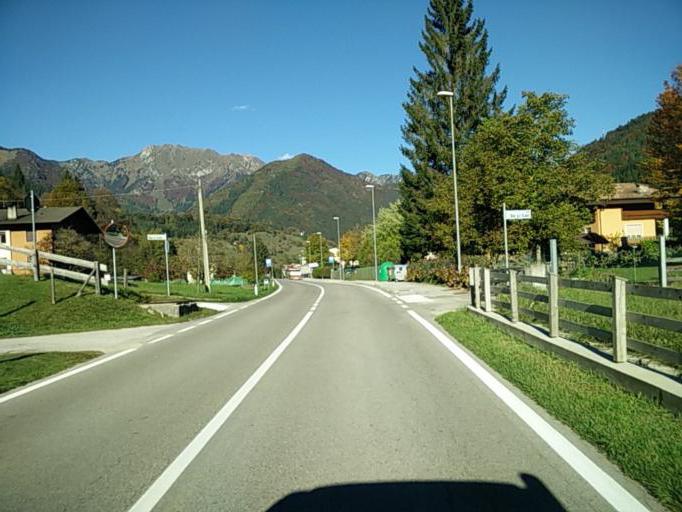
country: IT
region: Trentino-Alto Adige
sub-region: Provincia di Trento
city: Cimego
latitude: 45.8820
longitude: 10.6656
